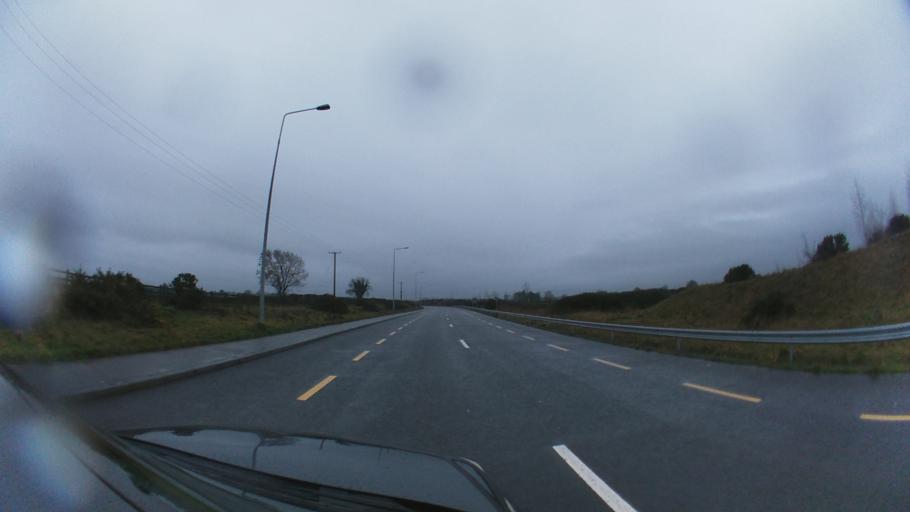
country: IE
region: Leinster
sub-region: County Carlow
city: Bagenalstown
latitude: 52.6780
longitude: -7.0323
